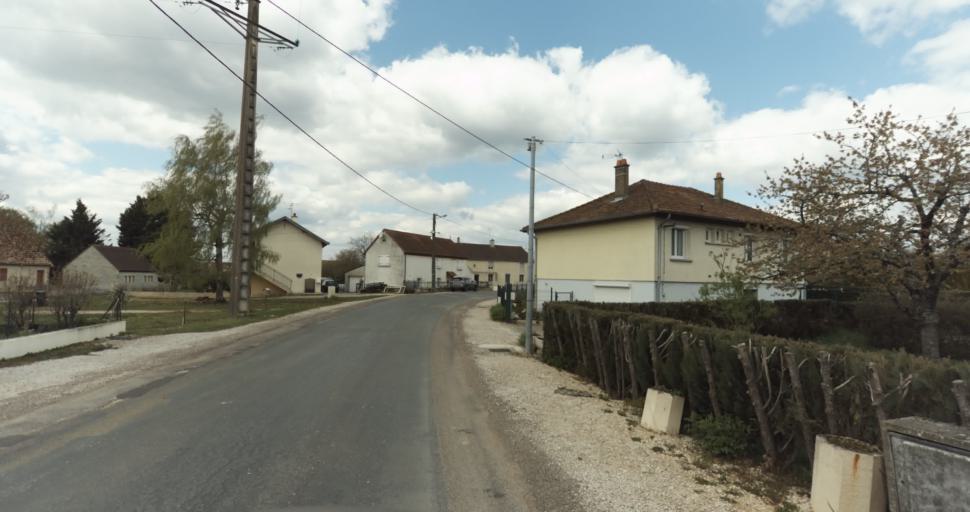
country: FR
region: Bourgogne
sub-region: Departement de la Cote-d'Or
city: Auxonne
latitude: 47.1874
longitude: 5.4034
